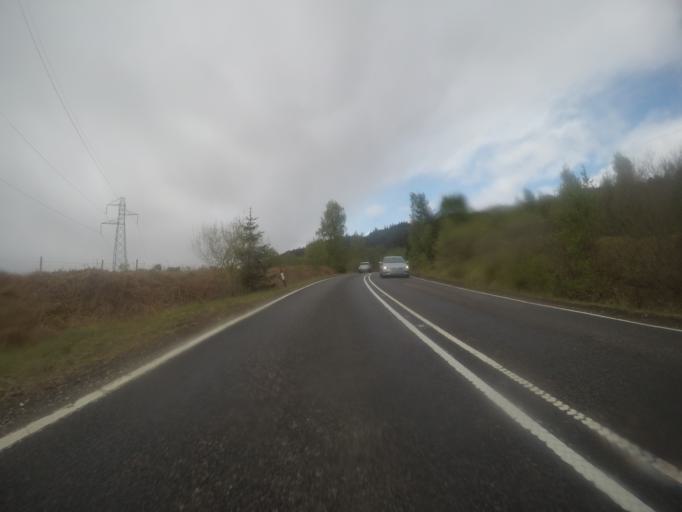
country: GB
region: Scotland
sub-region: Highland
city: Spean Bridge
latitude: 57.0833
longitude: -4.9076
